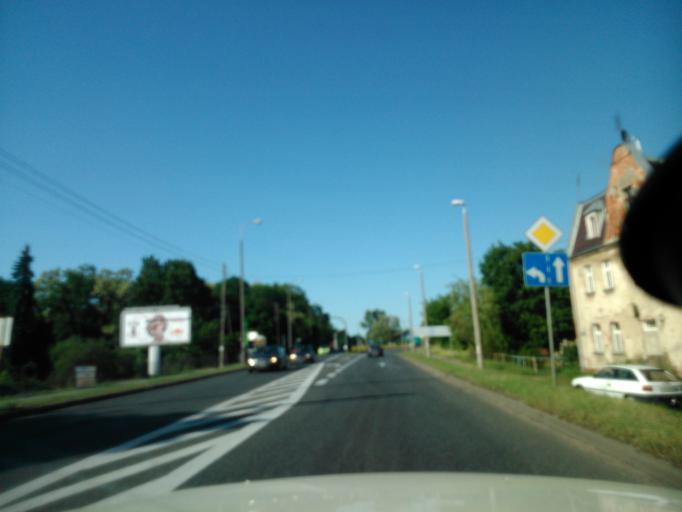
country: PL
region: Kujawsko-Pomorskie
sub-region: Torun
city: Torun
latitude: 52.9884
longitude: 18.5814
